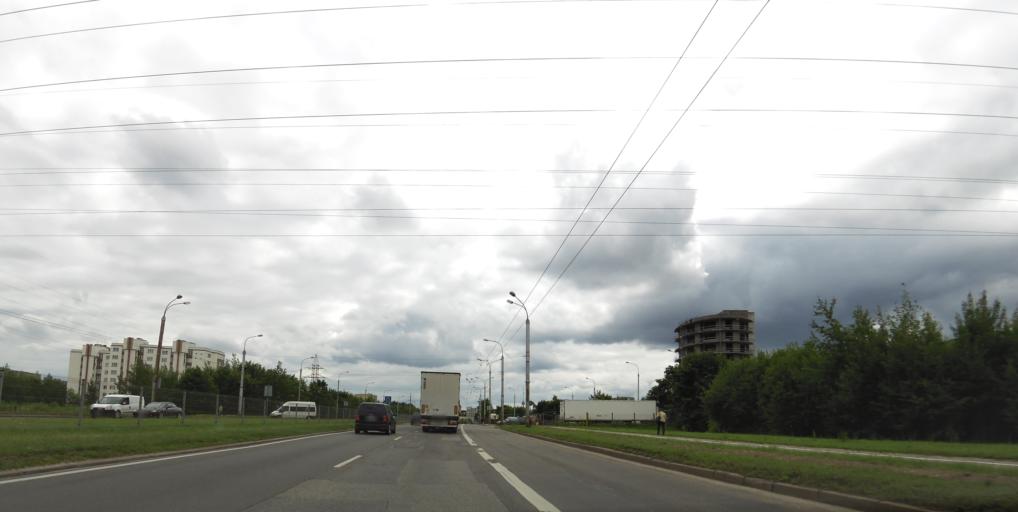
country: LT
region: Vilnius County
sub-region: Vilnius
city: Fabijoniskes
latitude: 54.7223
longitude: 25.2334
